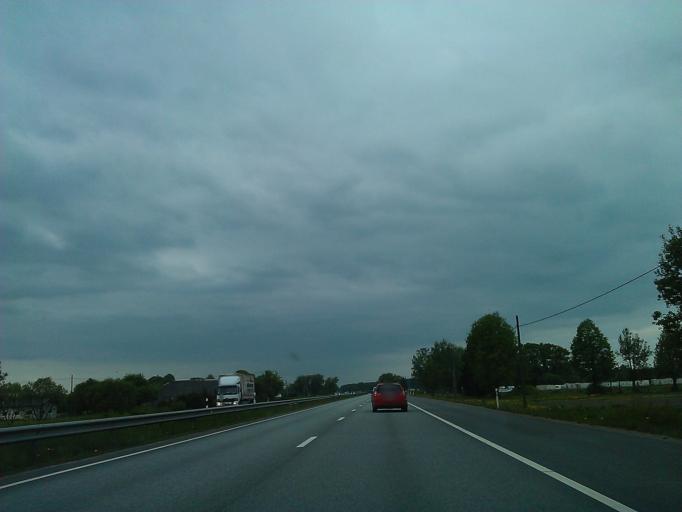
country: LV
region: Olaine
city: Olaine
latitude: 56.7770
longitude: 23.9362
